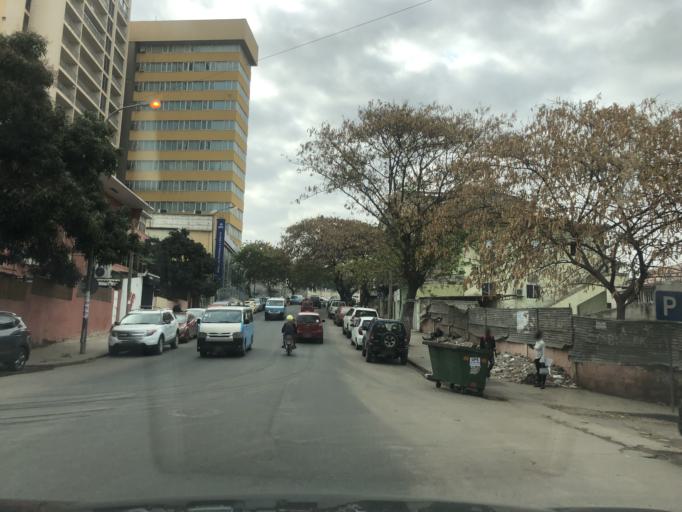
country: AO
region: Luanda
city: Luanda
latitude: -8.8245
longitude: 13.2327
